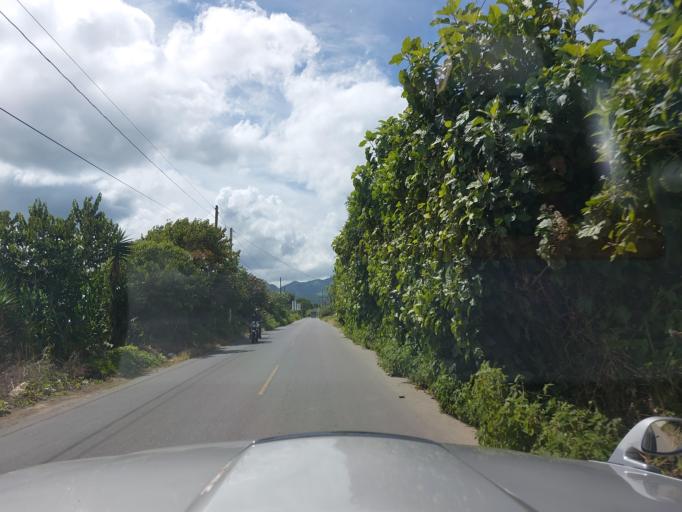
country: GT
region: Chimaltenango
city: Parramos
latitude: 14.6128
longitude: -90.8192
